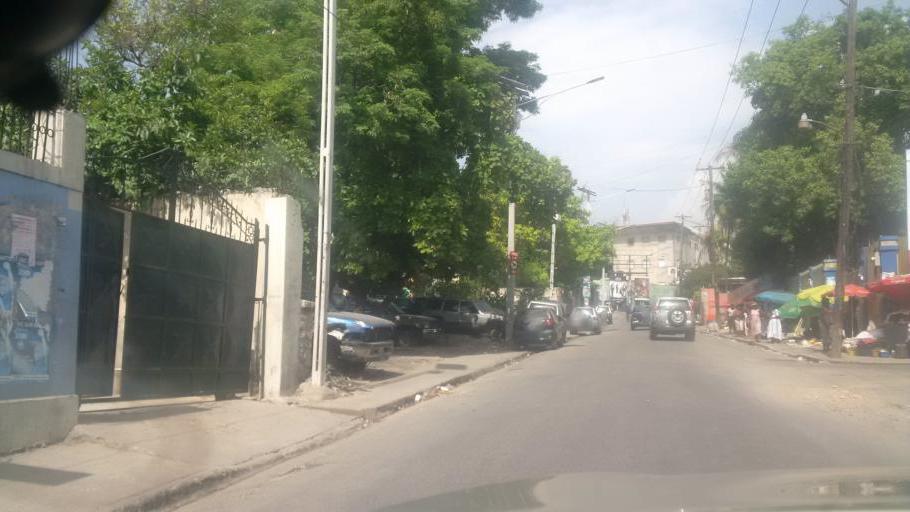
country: HT
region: Ouest
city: Port-au-Prince
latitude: 18.5336
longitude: -72.3199
